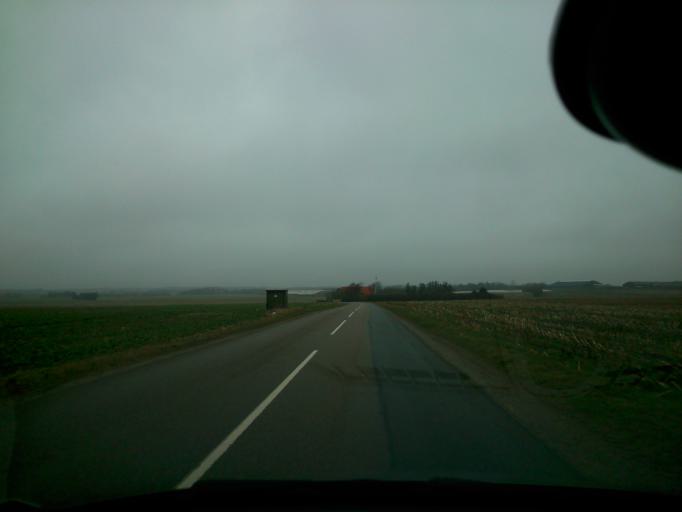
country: DK
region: Central Jutland
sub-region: Ringkobing-Skjern Kommune
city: Ringkobing
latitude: 56.0950
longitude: 8.4064
